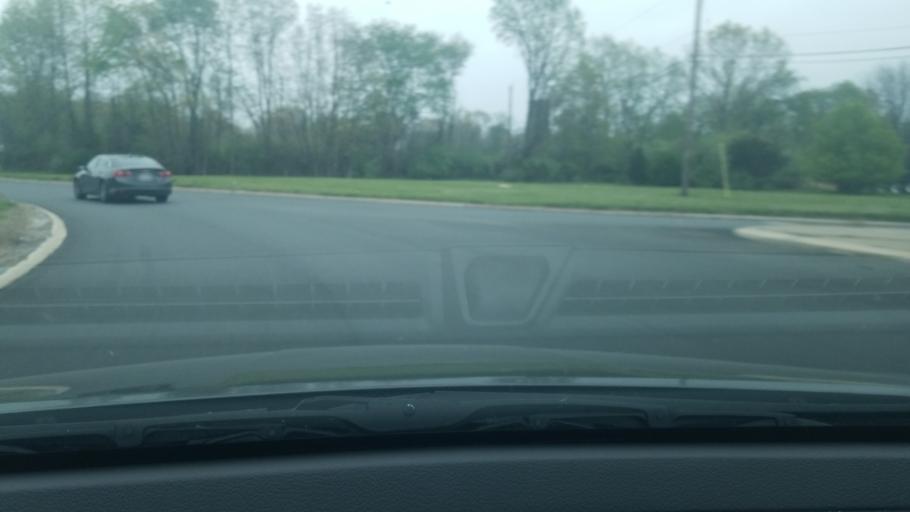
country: US
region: New Jersey
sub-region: Burlington County
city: Leisuretowne
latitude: 39.8866
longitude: -74.7409
